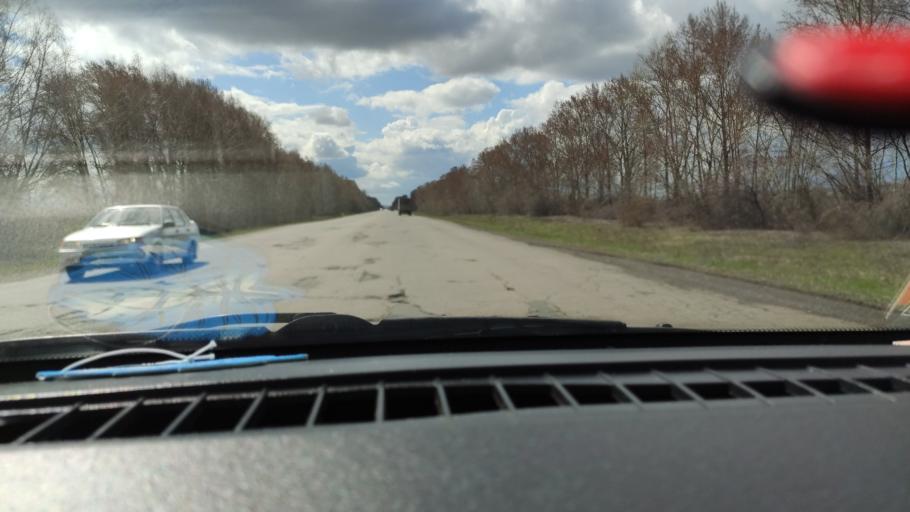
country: RU
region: Samara
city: Tol'yatti
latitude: 53.6362
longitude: 49.4189
